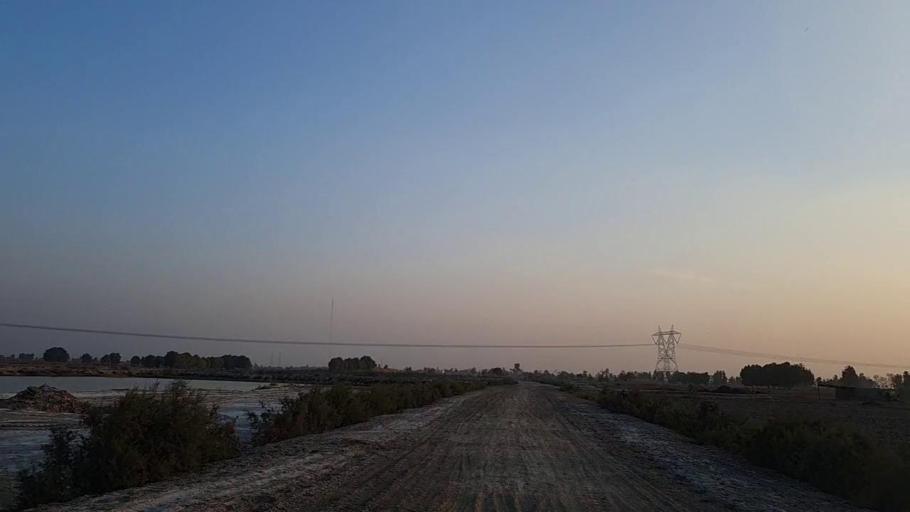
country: PK
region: Sindh
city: Naushahro Firoz
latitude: 26.7793
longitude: 68.0719
